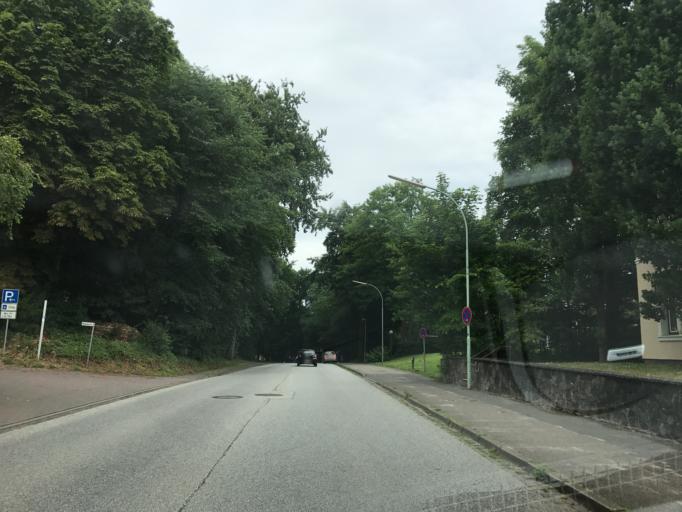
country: DE
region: Schleswig-Holstein
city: Meldorf
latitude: 54.0938
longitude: 9.0720
